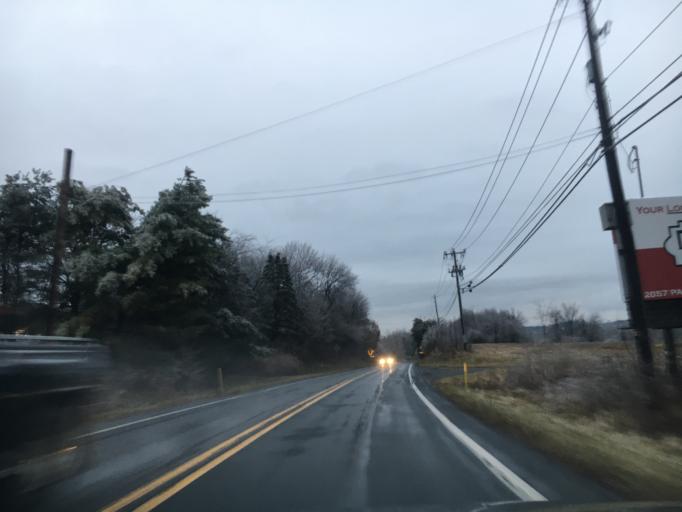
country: US
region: Pennsylvania
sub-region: Lehigh County
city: Schnecksville
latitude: 40.6342
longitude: -75.6068
